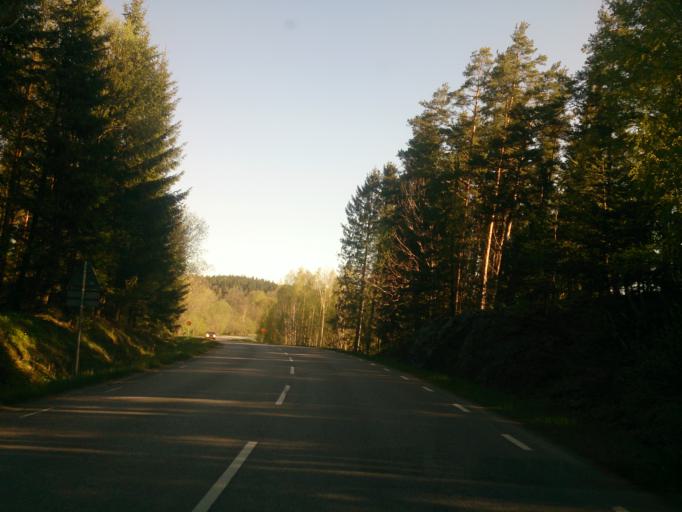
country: SE
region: OEstergoetland
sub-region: Linkopings Kommun
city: Berg
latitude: 58.5137
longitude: 15.5479
